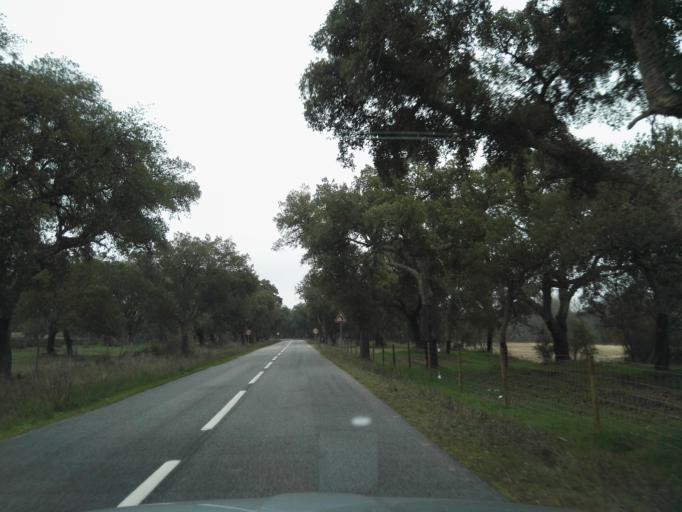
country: PT
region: Evora
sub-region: Vendas Novas
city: Vendas Novas
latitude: 38.7672
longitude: -8.3813
